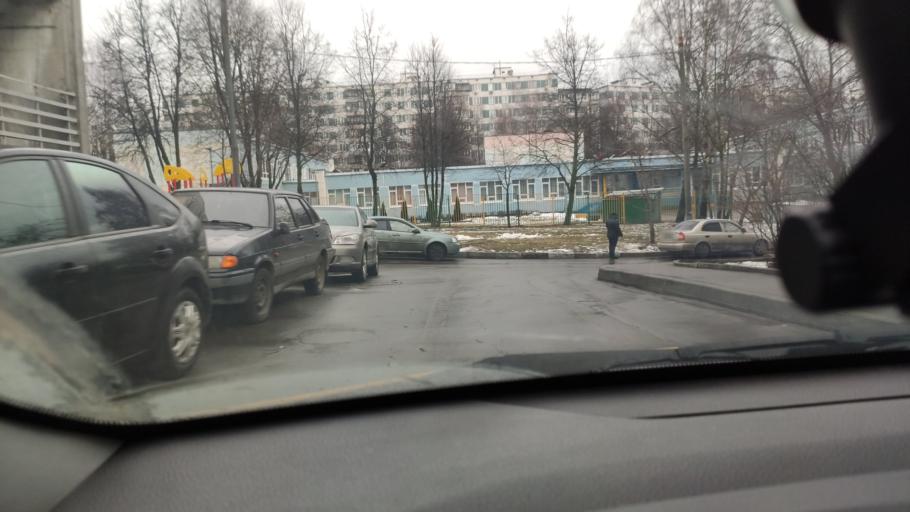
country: RU
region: Moscow
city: Orekhovo-Borisovo
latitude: 55.5984
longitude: 37.7150
